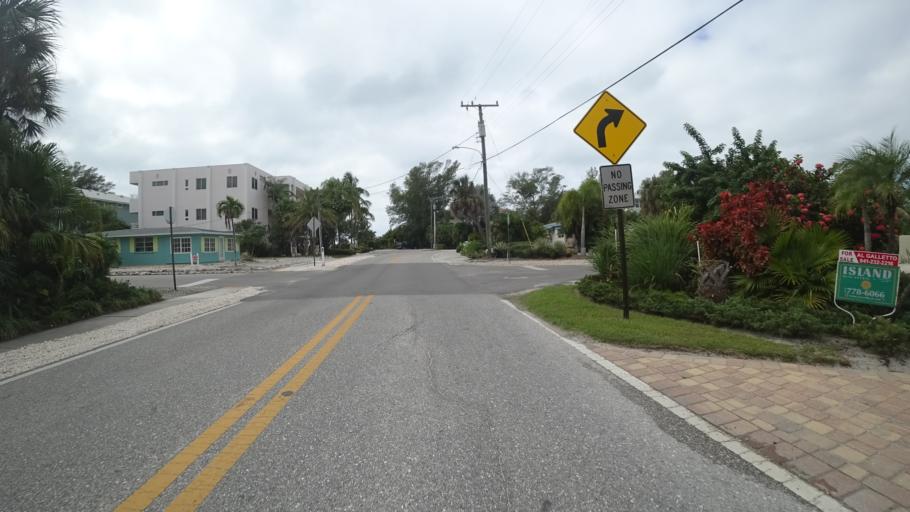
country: US
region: Florida
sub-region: Manatee County
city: Holmes Beach
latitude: 27.4950
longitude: -82.7099
